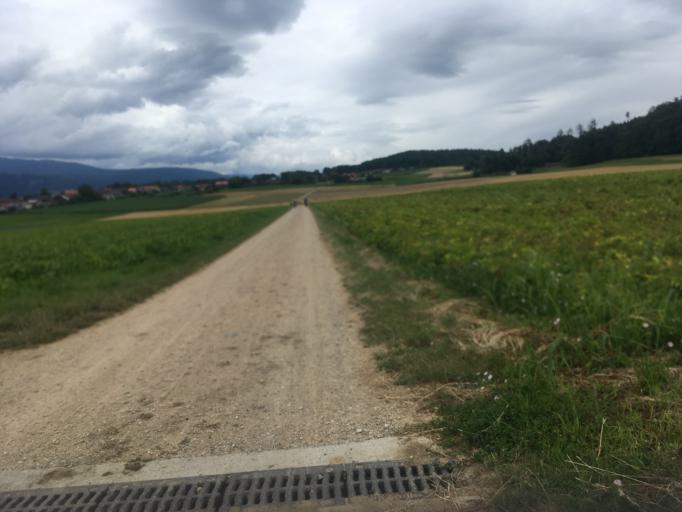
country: CH
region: Bern
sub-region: Seeland District
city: Ins
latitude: 47.0239
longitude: 7.1053
